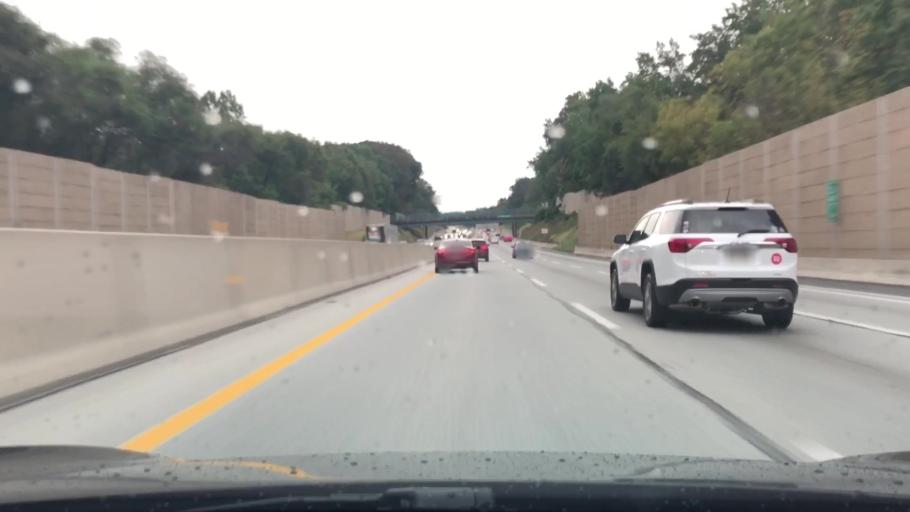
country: US
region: Pennsylvania
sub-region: Bucks County
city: Churchville
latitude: 40.1572
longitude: -75.0373
